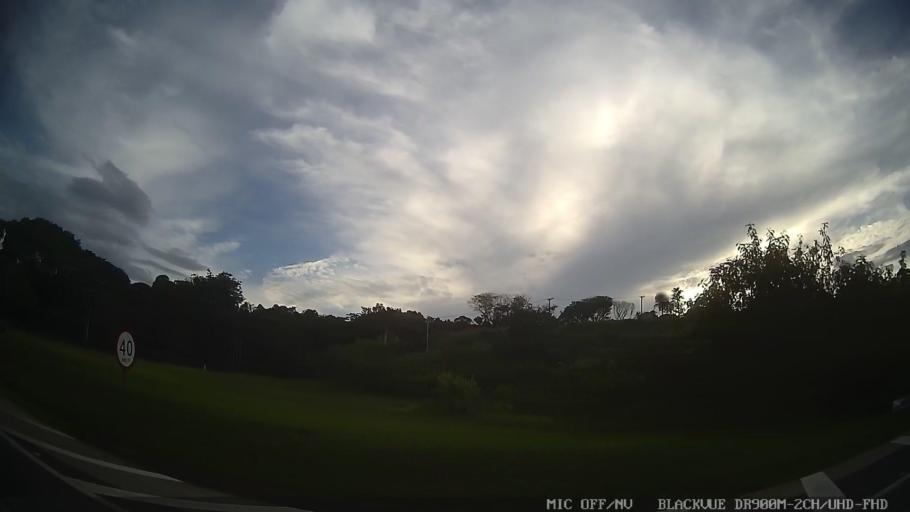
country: BR
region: Sao Paulo
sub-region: Porto Feliz
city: Porto Feliz
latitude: -23.2258
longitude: -47.5698
